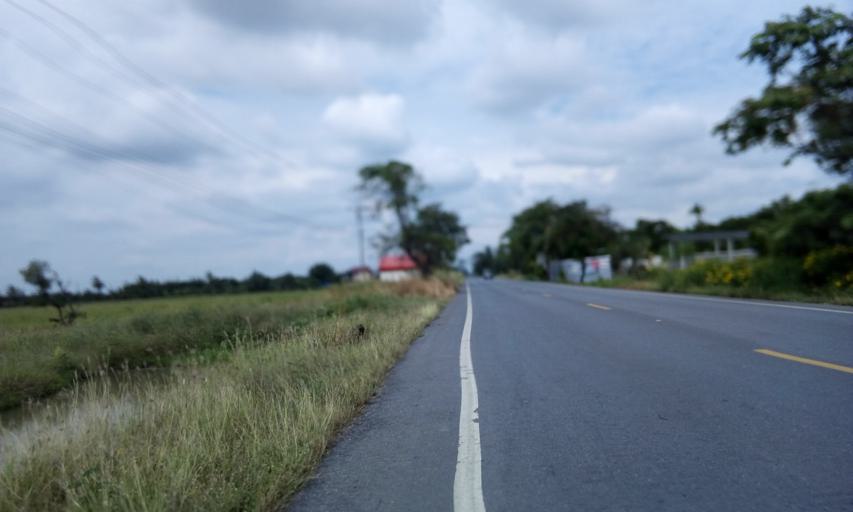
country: TH
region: Pathum Thani
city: Ban Lam Luk Ka
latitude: 14.0283
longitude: 100.8437
